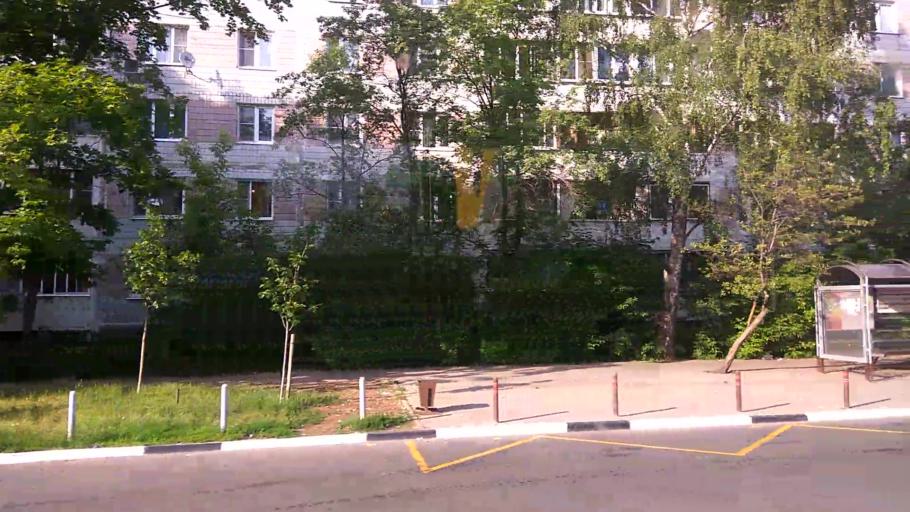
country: RU
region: Moskovskaya
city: Mytishchi
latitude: 55.9049
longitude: 37.7111
